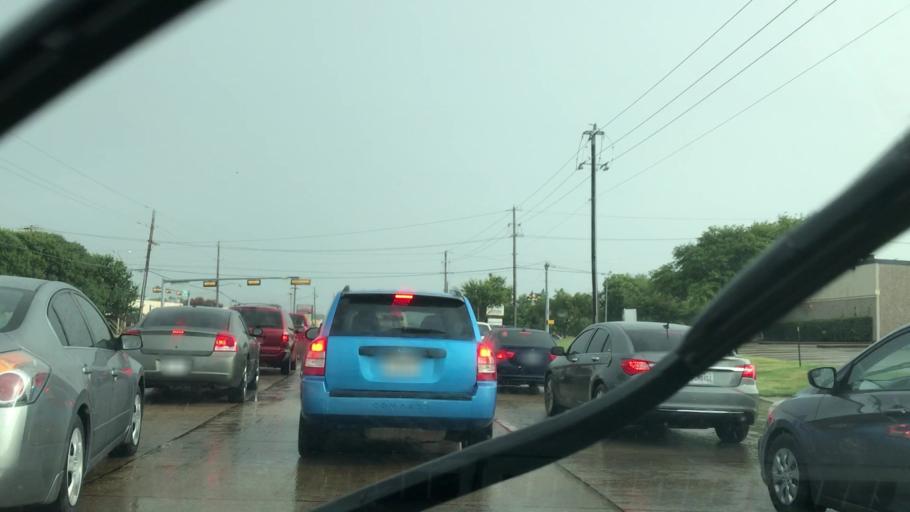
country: US
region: Texas
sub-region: Dallas County
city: Richardson
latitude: 32.8954
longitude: -96.7006
